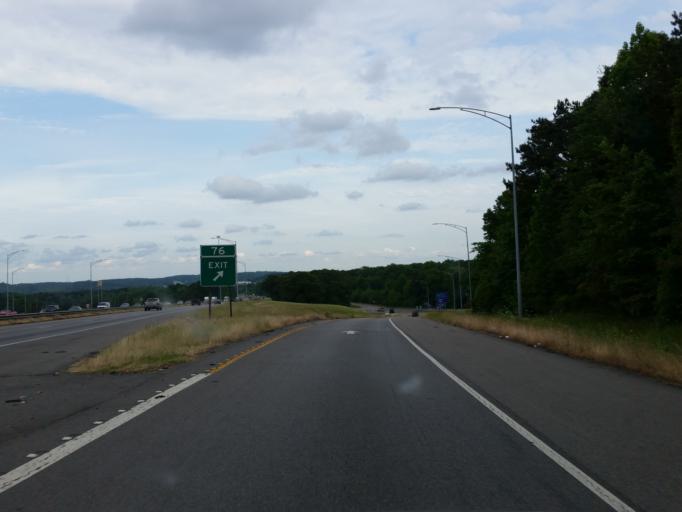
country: US
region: Alabama
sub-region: Tuscaloosa County
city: Holt
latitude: 33.1747
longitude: -87.4797
